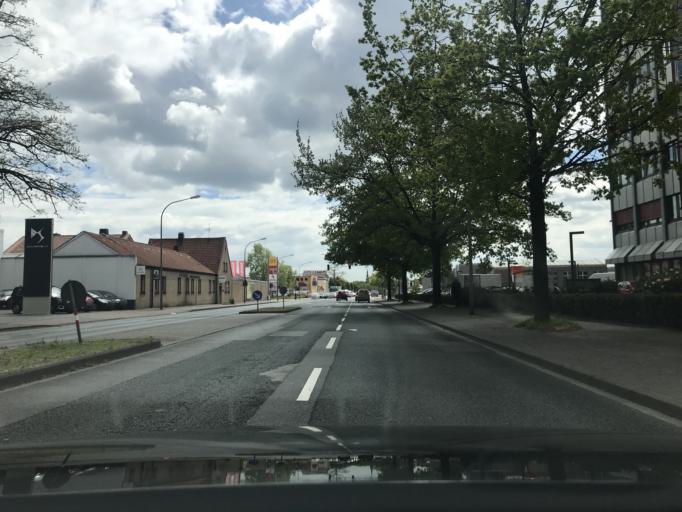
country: DE
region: Lower Saxony
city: Osnabrueck
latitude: 52.2936
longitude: 8.0356
